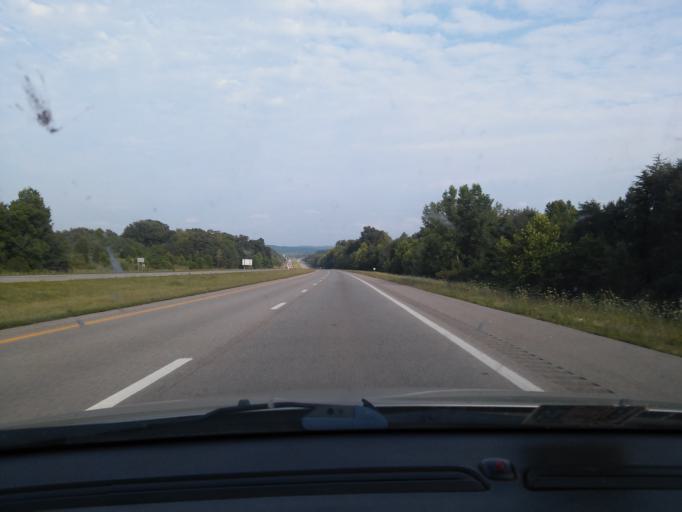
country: US
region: Ohio
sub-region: Gallia County
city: Gallipolis
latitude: 38.8719
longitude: -82.2813
